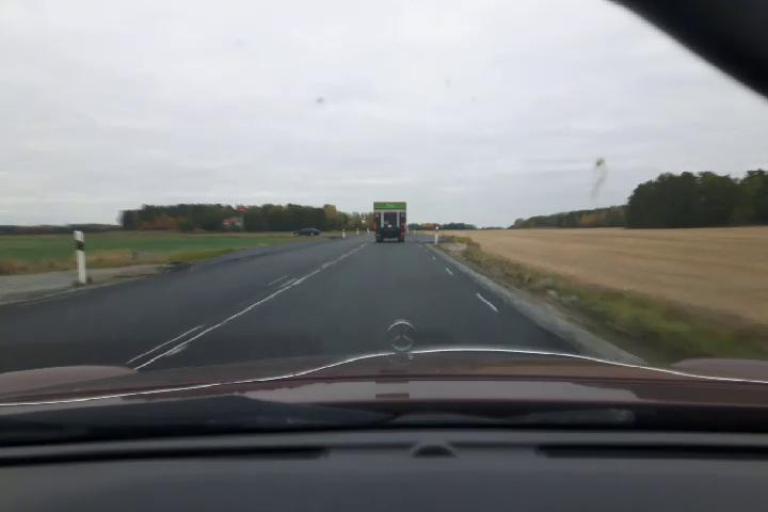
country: SE
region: Uppsala
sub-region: Enkopings Kommun
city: Enkoping
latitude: 59.6008
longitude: 17.0187
